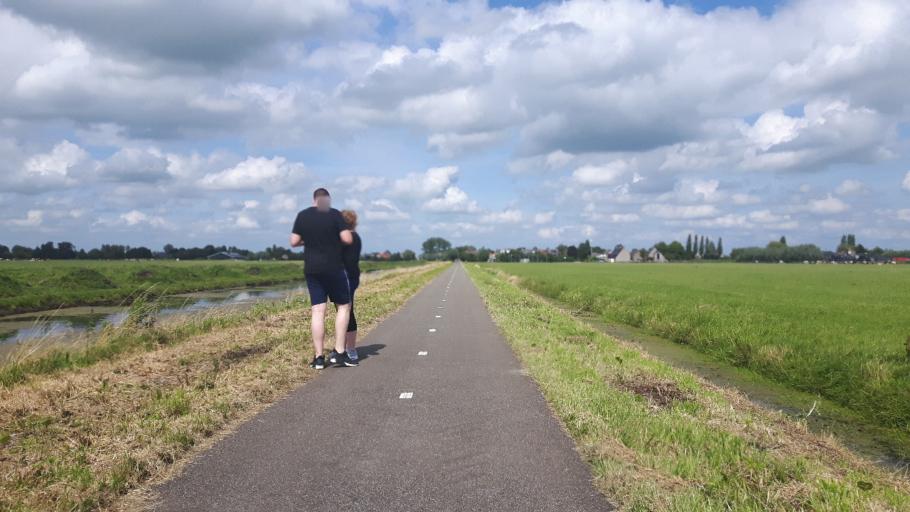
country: NL
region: South Holland
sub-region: Gemeente Vlist
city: Vlist
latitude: 51.9714
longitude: 4.8144
